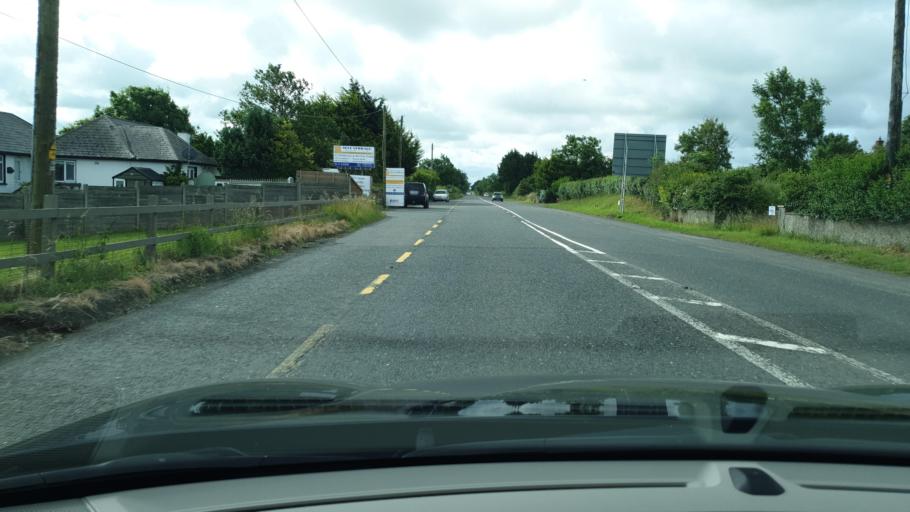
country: IE
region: Leinster
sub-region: An Mhi
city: Ashbourne
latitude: 53.4933
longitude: -6.3814
